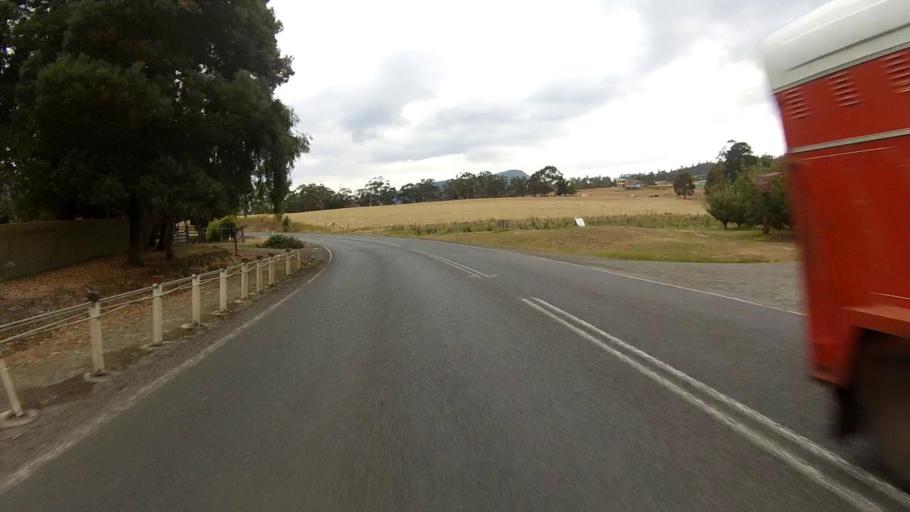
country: AU
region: Tasmania
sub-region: Huon Valley
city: Franklin
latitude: -43.0884
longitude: 147.0292
